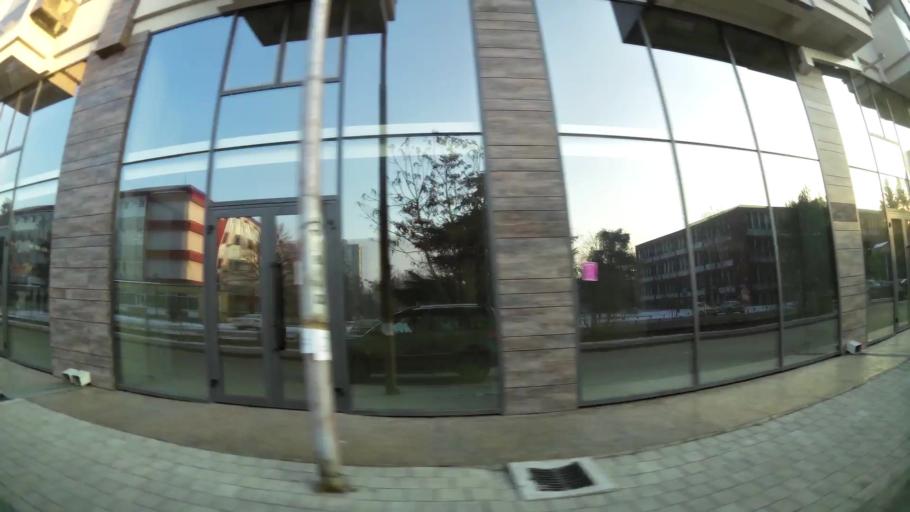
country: MK
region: Karpos
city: Skopje
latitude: 42.0055
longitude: 21.4091
